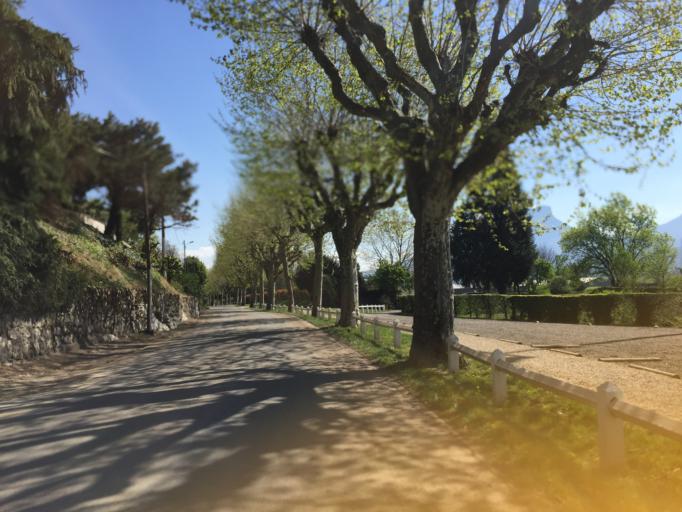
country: FR
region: Rhone-Alpes
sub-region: Departement de la Savoie
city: Barby
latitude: 45.5629
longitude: 5.9819
